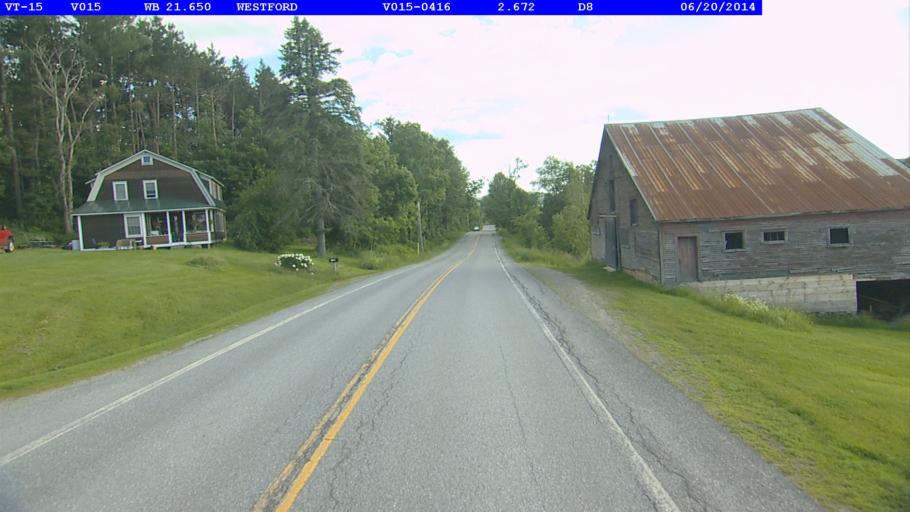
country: US
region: Vermont
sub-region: Chittenden County
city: Jericho
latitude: 44.6298
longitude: -72.9176
